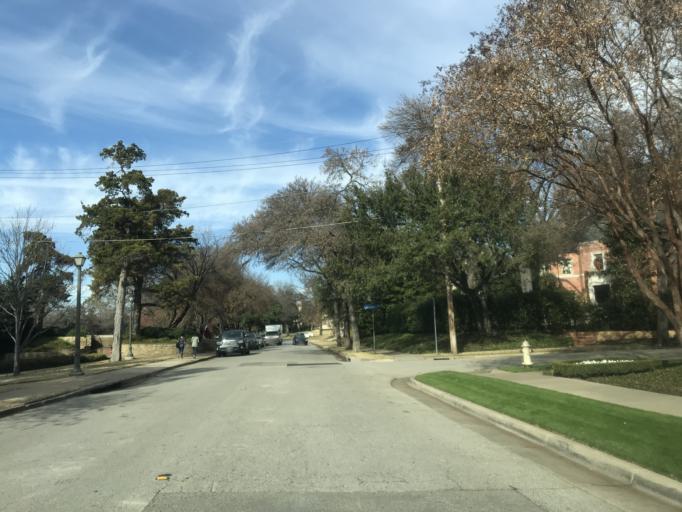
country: US
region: Texas
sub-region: Dallas County
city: Highland Park
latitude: 32.8264
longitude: -96.8008
